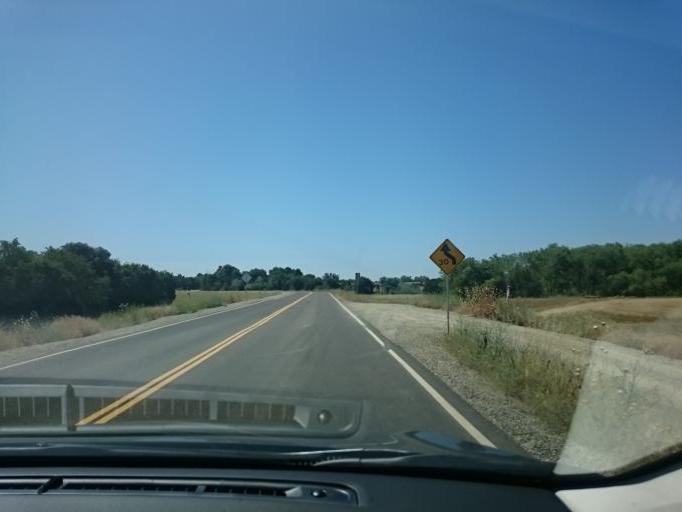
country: US
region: California
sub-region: Yolo County
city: West Sacramento
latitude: 38.5584
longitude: -121.5183
